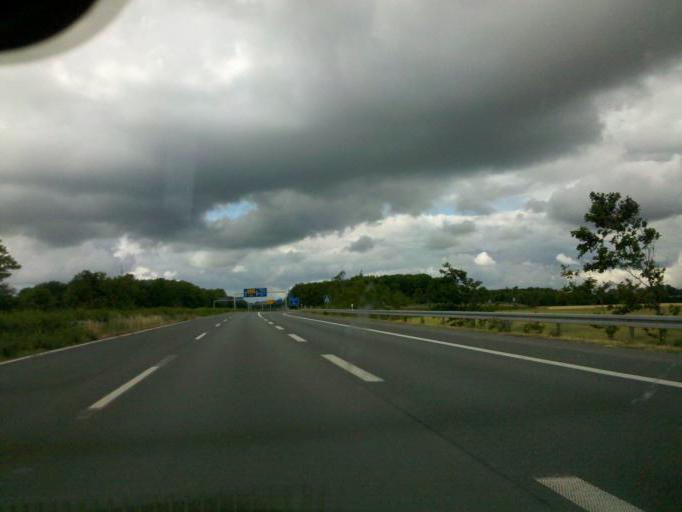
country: DE
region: North Rhine-Westphalia
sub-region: Regierungsbezirk Arnsberg
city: Anrochte
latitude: 51.5875
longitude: 8.3139
